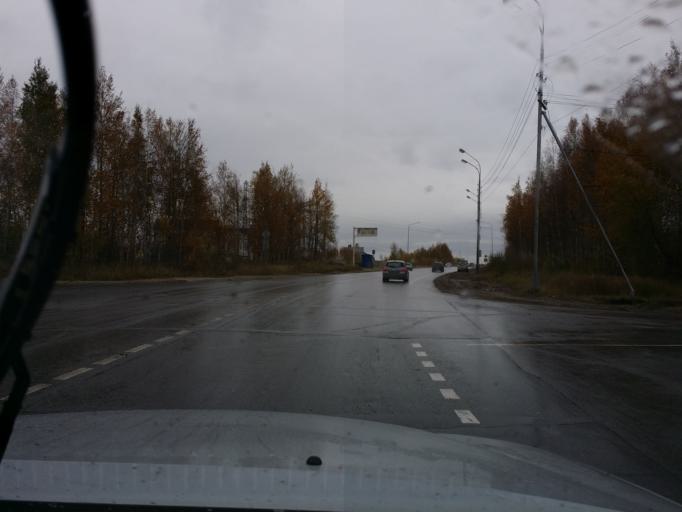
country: RU
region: Khanty-Mansiyskiy Avtonomnyy Okrug
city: Megion
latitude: 61.0497
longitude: 76.1119
